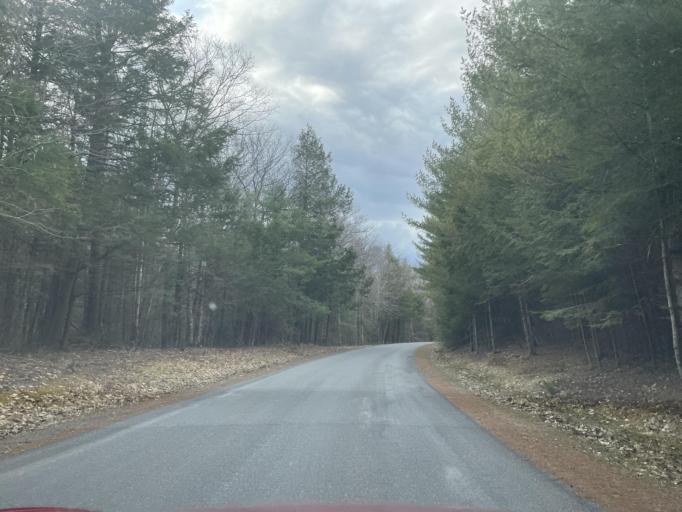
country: US
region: New York
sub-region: Greene County
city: Palenville
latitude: 42.1969
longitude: -74.0527
